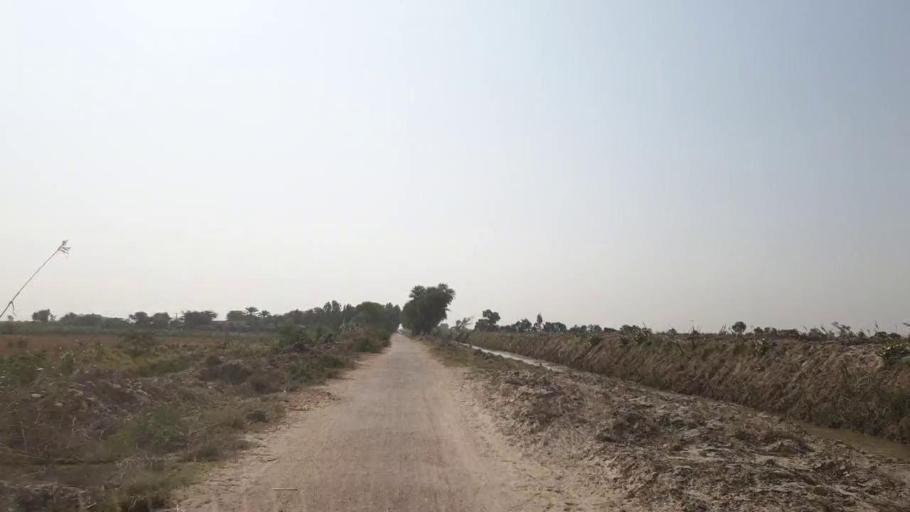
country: PK
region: Sindh
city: Bulri
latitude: 24.9670
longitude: 68.3942
